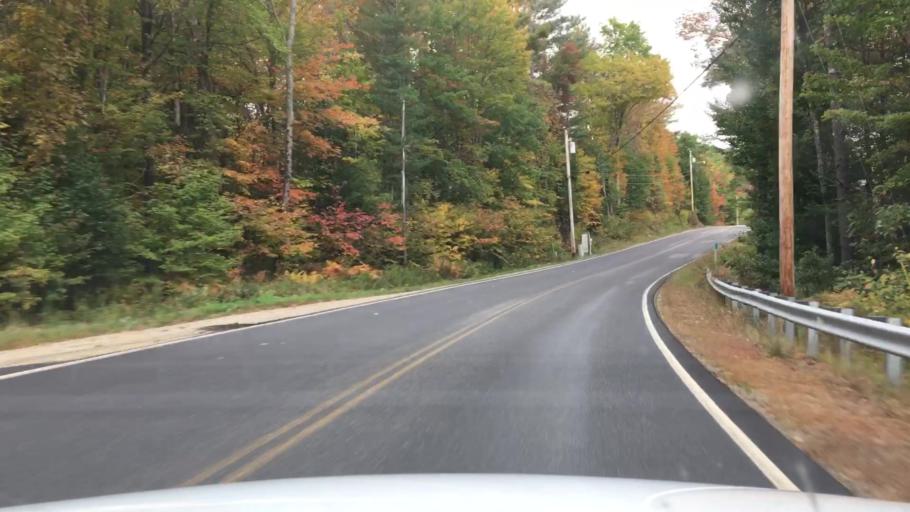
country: US
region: Maine
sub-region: Oxford County
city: Bethel
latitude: 44.2765
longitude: -70.7316
